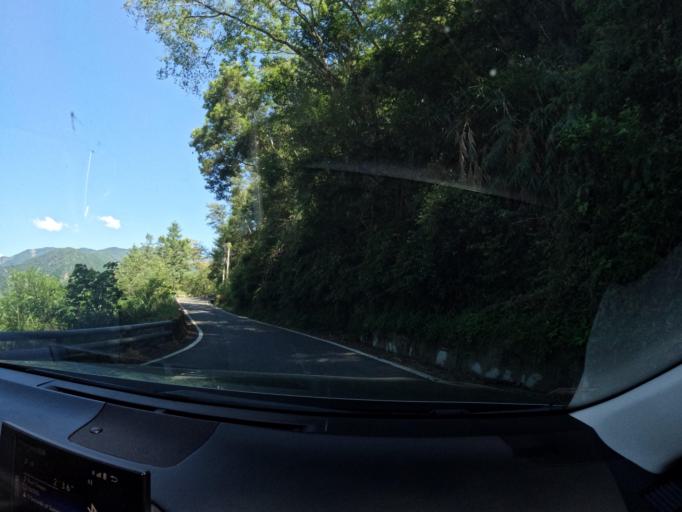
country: TW
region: Taiwan
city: Yujing
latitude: 23.2796
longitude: 120.8757
